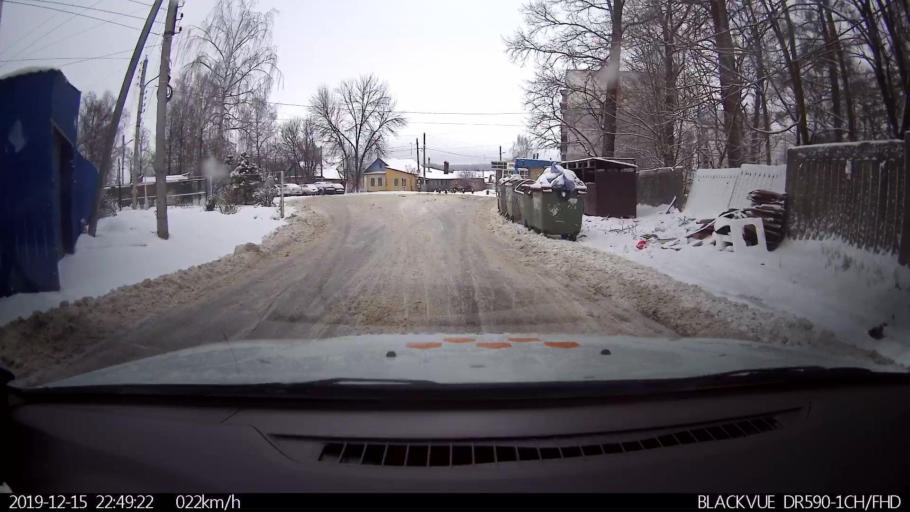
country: RU
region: Nizjnij Novgorod
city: Nizhniy Novgorod
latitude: 56.2344
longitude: 43.9780
